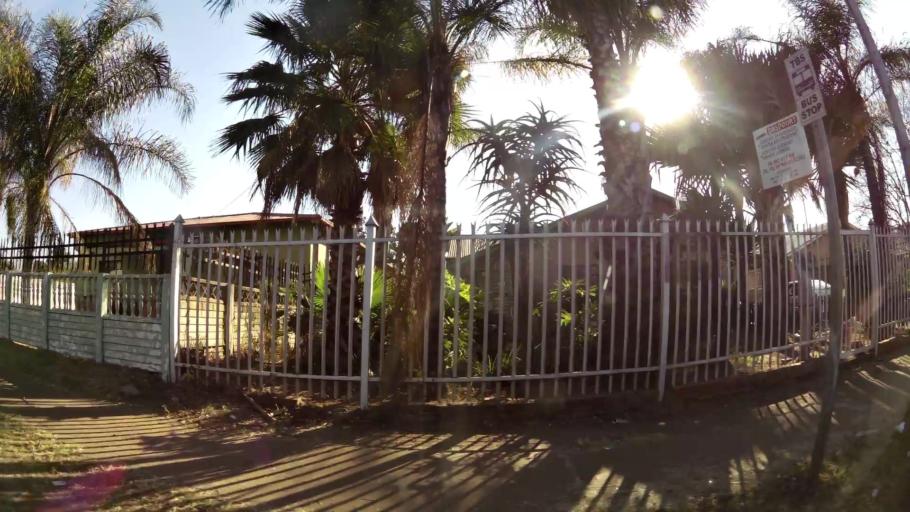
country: ZA
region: Gauteng
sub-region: City of Tshwane Metropolitan Municipality
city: Pretoria
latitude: -25.7093
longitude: 28.1550
